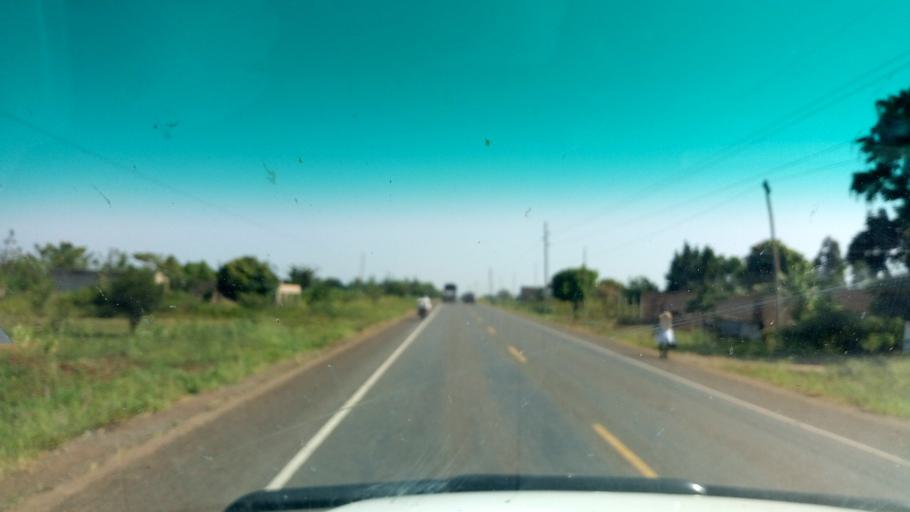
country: UG
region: Western Region
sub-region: Kiryandongo District
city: Kiryandongo
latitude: 1.9342
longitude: 32.1246
